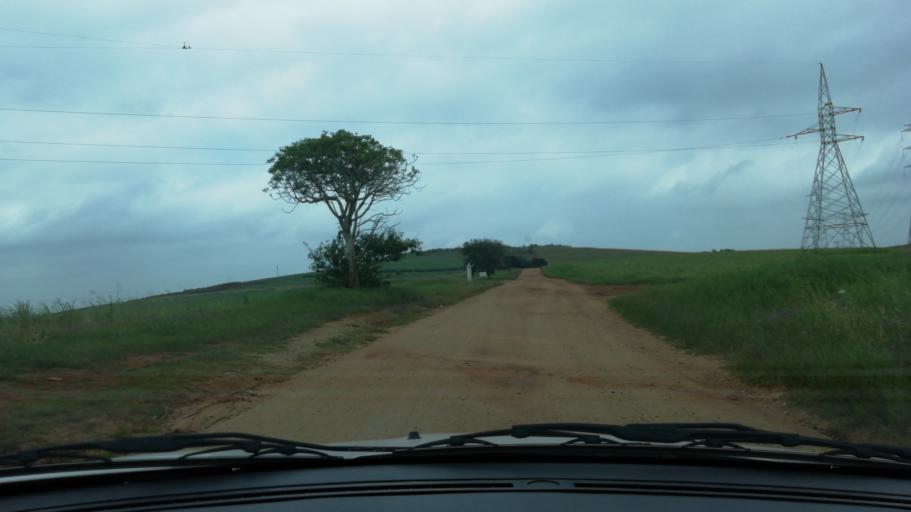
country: ZA
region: KwaZulu-Natal
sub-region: uThungulu District Municipality
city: Empangeni
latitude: -28.7314
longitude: 31.9016
